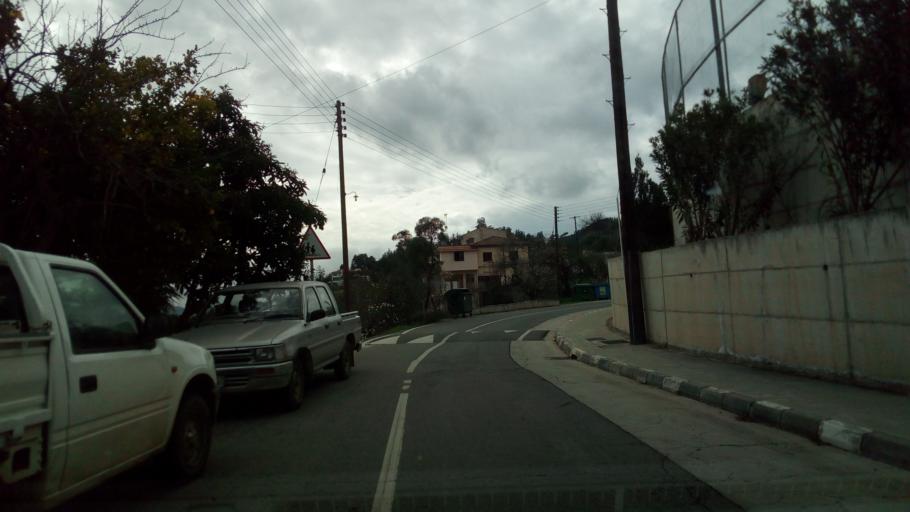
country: CY
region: Lefkosia
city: Klirou
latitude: 34.9968
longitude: 33.1207
